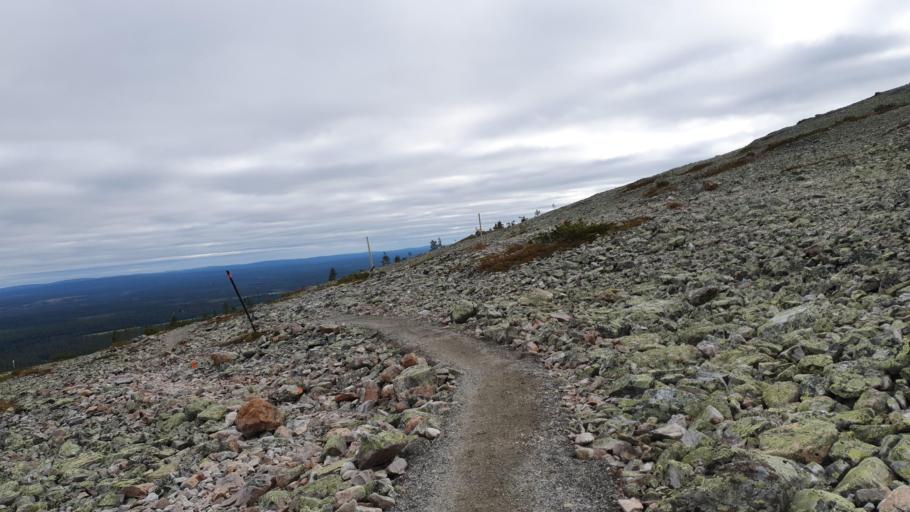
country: FI
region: Lapland
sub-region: Tunturi-Lappi
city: Kolari
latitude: 67.5652
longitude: 24.2511
